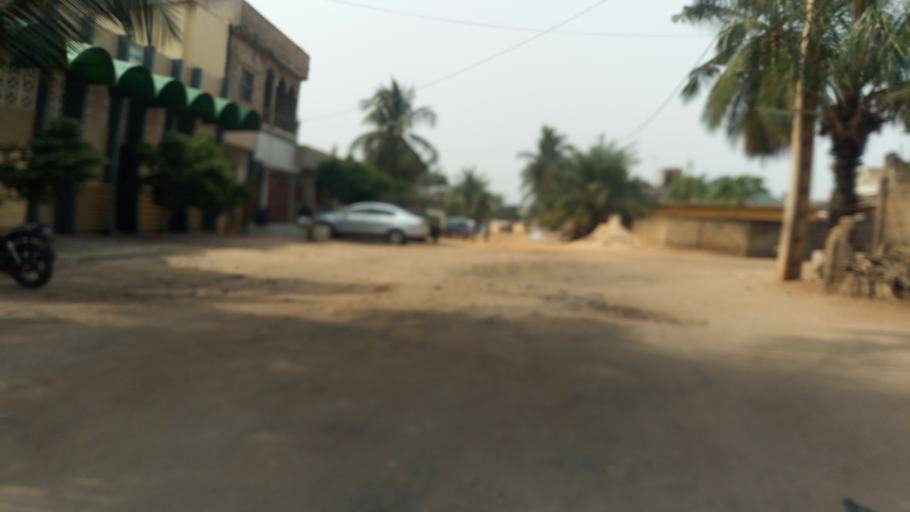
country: TG
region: Maritime
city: Lome
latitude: 6.1749
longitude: 1.1740
